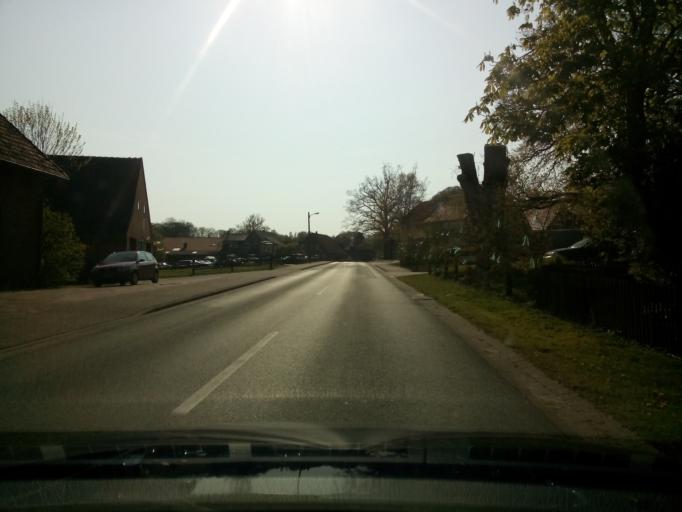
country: DE
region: Lower Saxony
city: Bruchhausen-Vilsen
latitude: 52.8120
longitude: 8.9928
